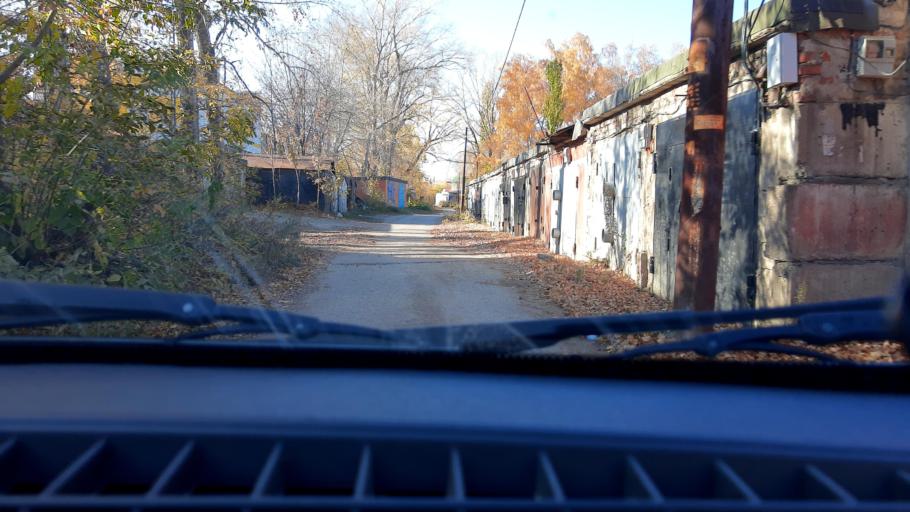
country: RU
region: Bashkortostan
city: Ufa
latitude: 54.8362
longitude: 56.1200
